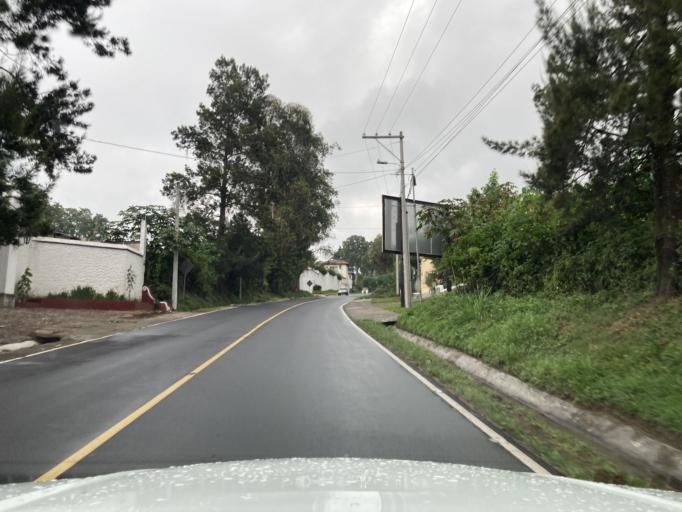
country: GT
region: Sacatepequez
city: San Miguel Duenas
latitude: 14.5183
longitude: -90.7840
